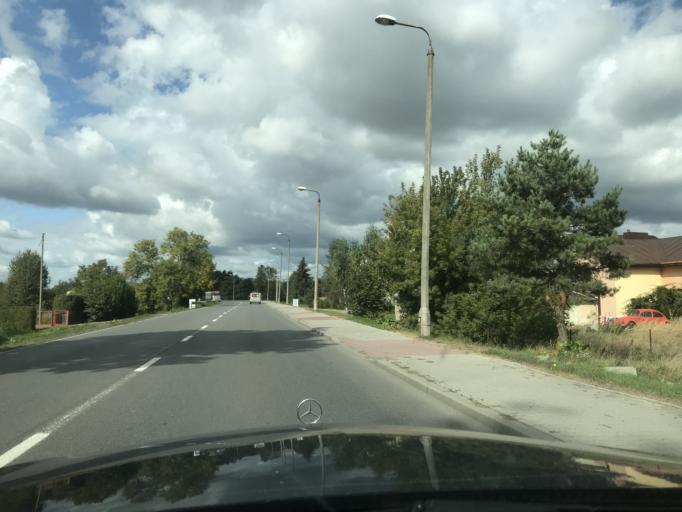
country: PL
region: Lublin Voivodeship
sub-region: Powiat krasnicki
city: Krasnik
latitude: 50.9075
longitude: 22.2653
